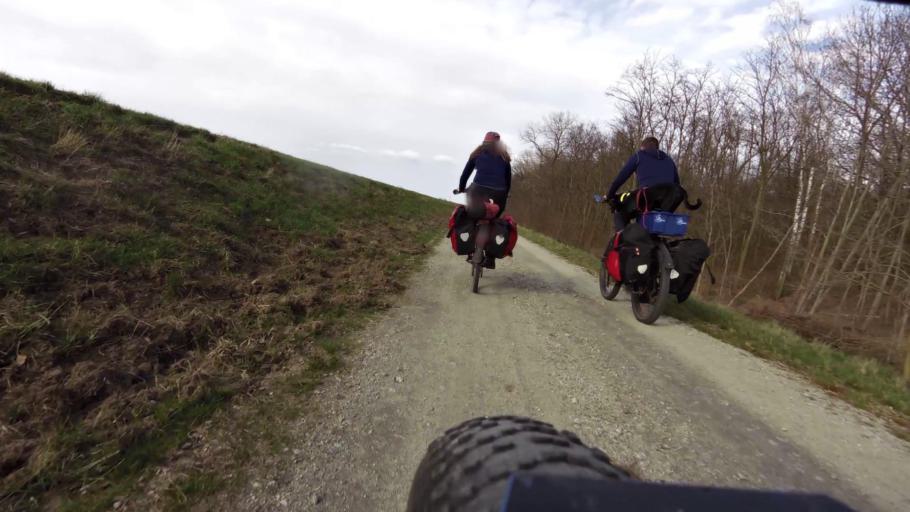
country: DE
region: Brandenburg
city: Reitwein
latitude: 52.5292
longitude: 14.6107
